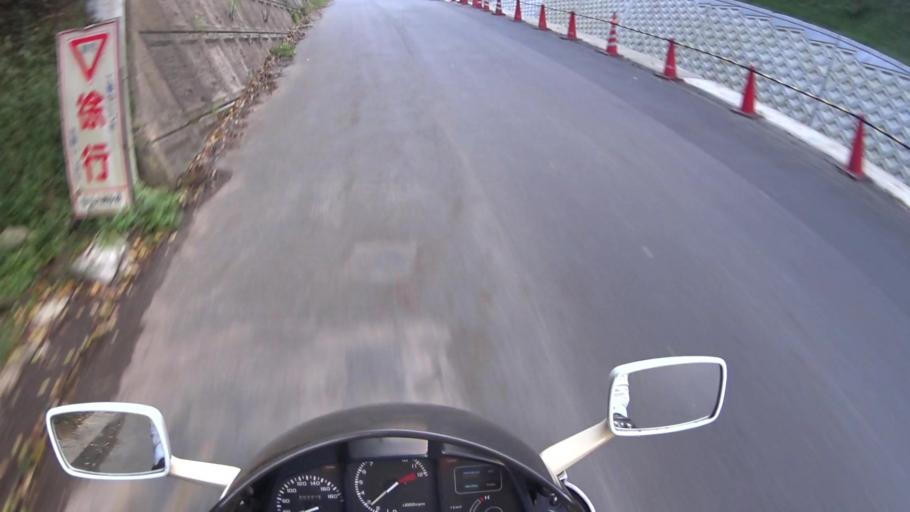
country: JP
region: Kyoto
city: Uji
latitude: 34.9196
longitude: 135.8268
